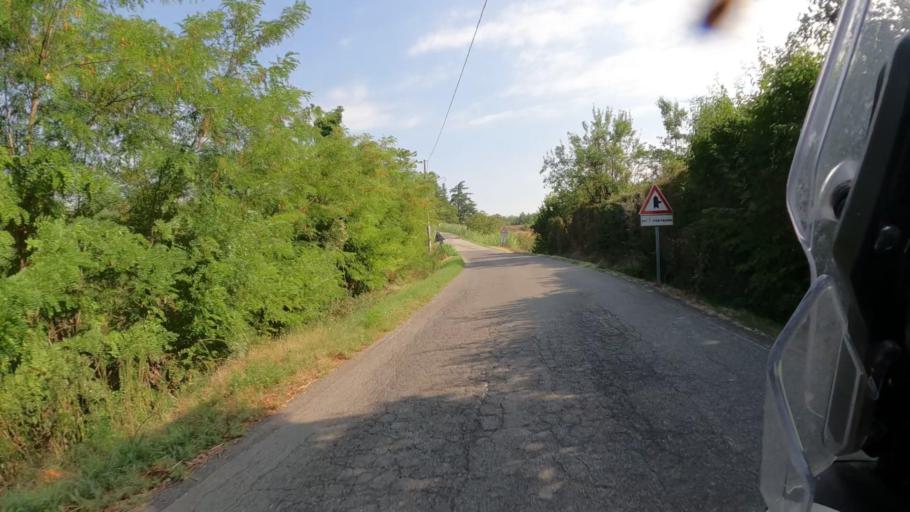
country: IT
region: Piedmont
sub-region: Provincia di Alessandria
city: Altavilla Monferrato
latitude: 44.9675
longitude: 8.3868
